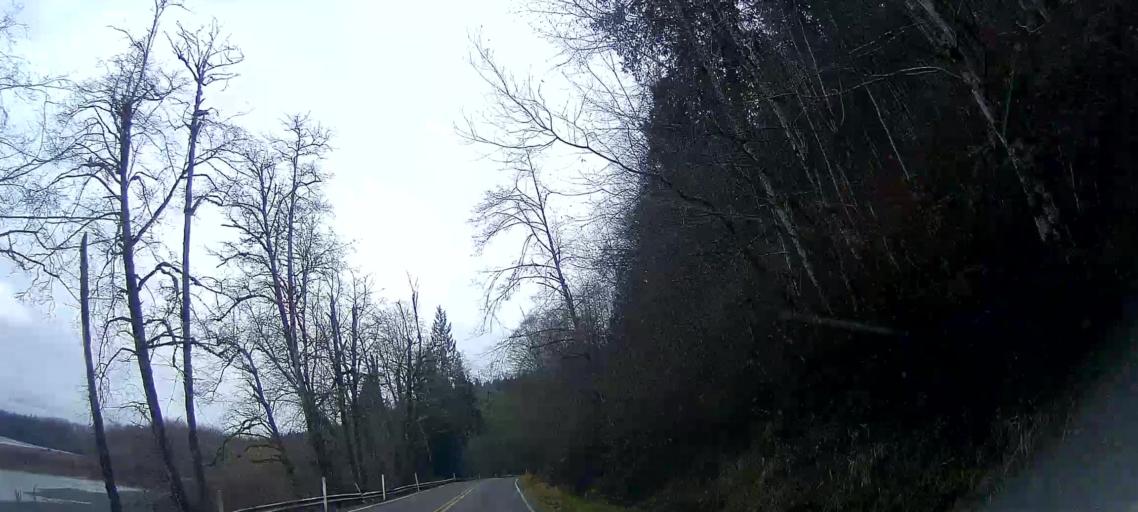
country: US
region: Washington
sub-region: Skagit County
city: Sedro-Woolley
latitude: 48.5096
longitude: -121.8982
